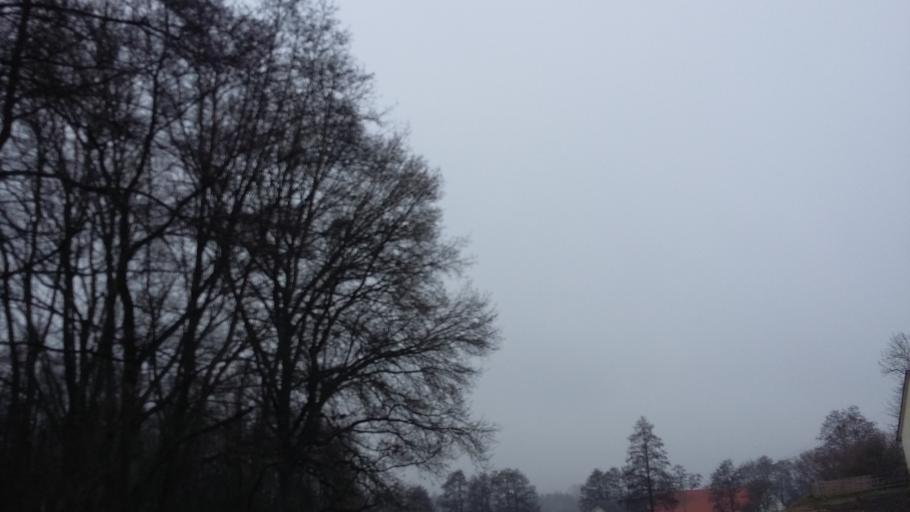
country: DE
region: Bavaria
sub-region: Swabia
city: Pottmes
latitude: 48.5701
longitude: 11.0979
